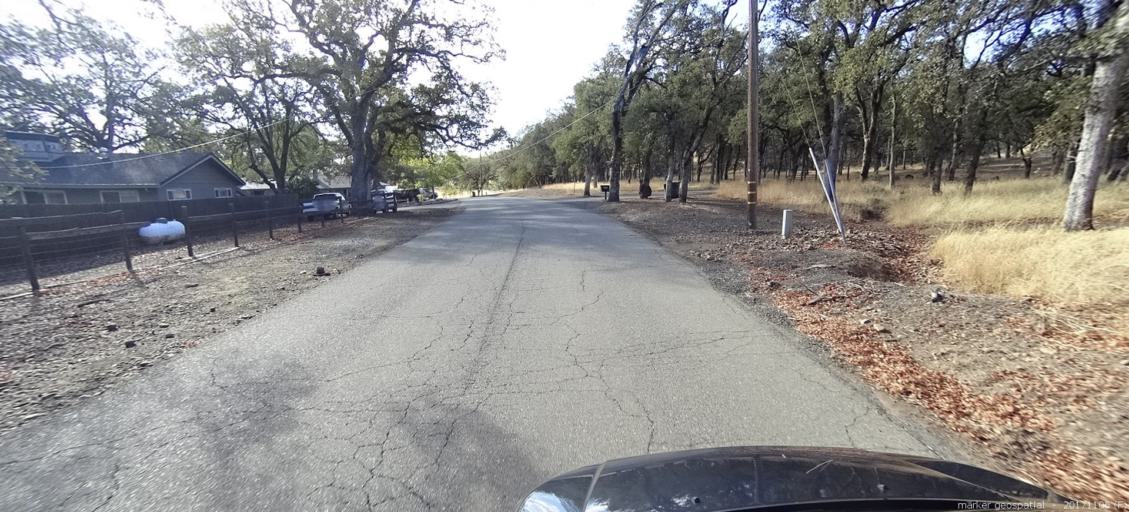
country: US
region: California
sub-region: Shasta County
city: Palo Cedro
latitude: 40.5408
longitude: -122.2488
